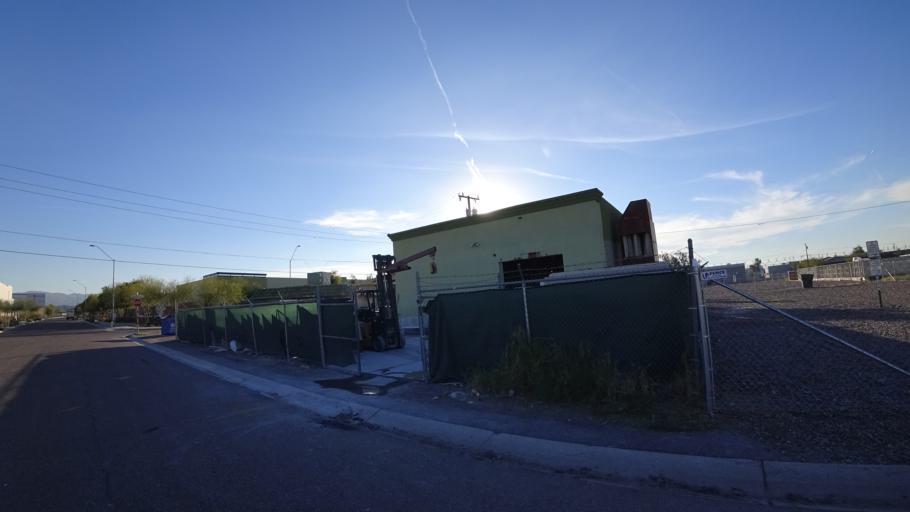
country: US
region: Arizona
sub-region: Maricopa County
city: Phoenix
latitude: 33.4243
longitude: -112.0424
